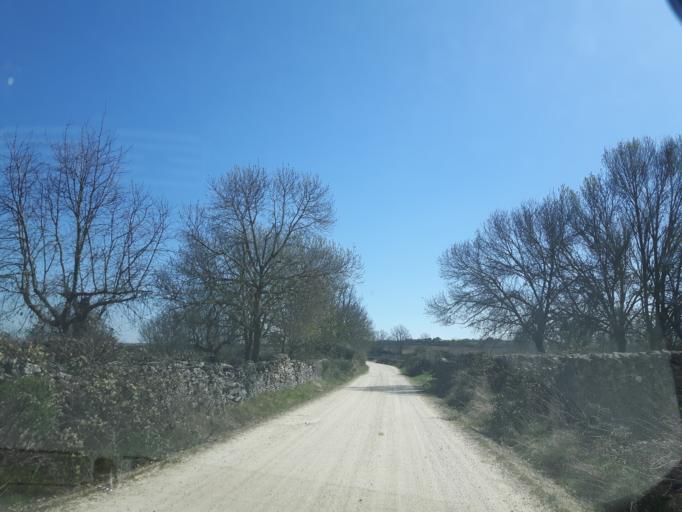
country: ES
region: Castille and Leon
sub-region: Provincia de Salamanca
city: Bermellar
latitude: 40.9619
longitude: -6.6744
